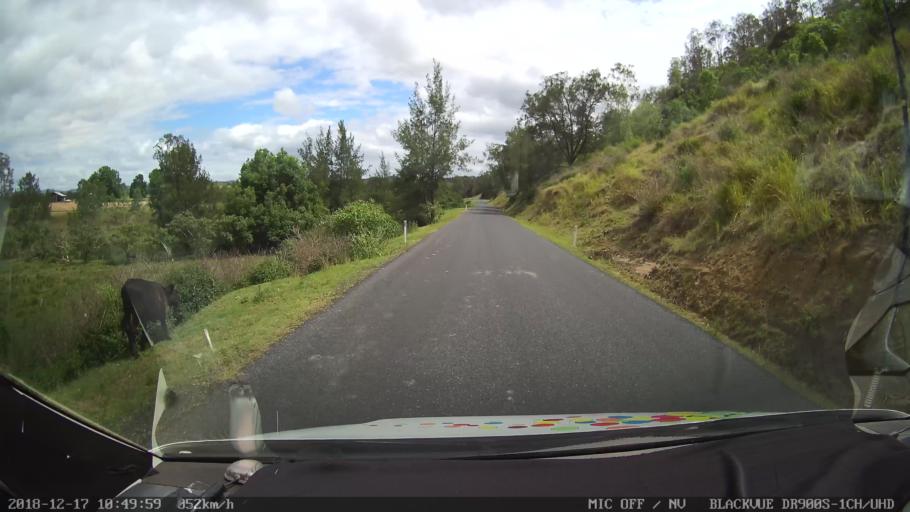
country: AU
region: New South Wales
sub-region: Clarence Valley
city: Gordon
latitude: -28.8620
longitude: 152.5738
